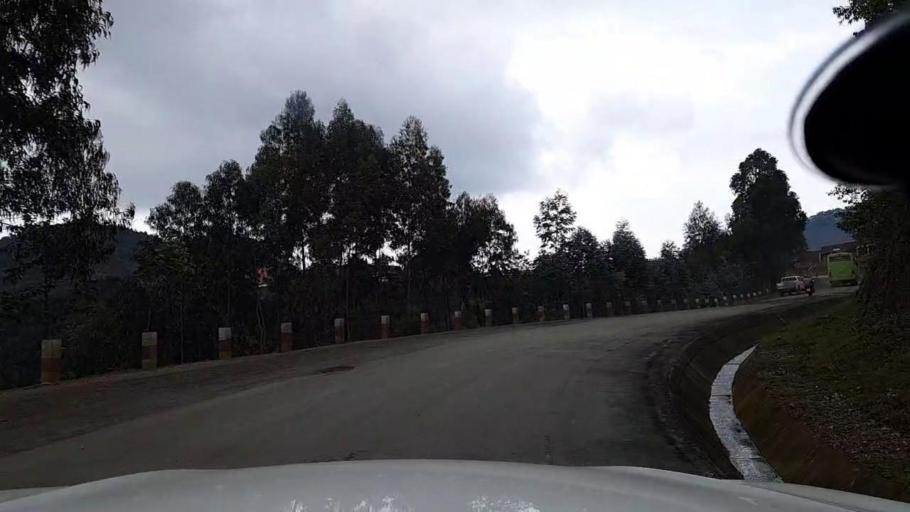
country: RW
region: Western Province
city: Kibuye
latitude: -2.0588
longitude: 29.5124
